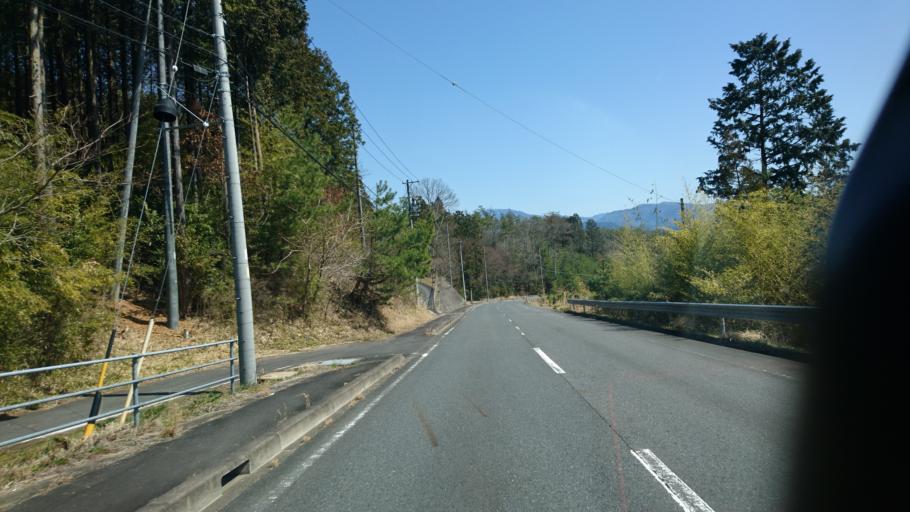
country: JP
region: Gifu
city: Nakatsugawa
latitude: 35.4604
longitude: 137.3641
